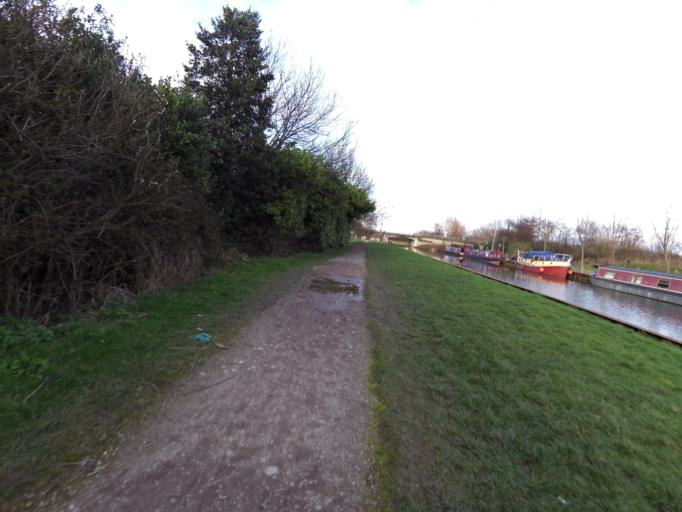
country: GB
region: England
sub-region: North Yorkshire
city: Selby
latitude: 53.7760
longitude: -1.0645
